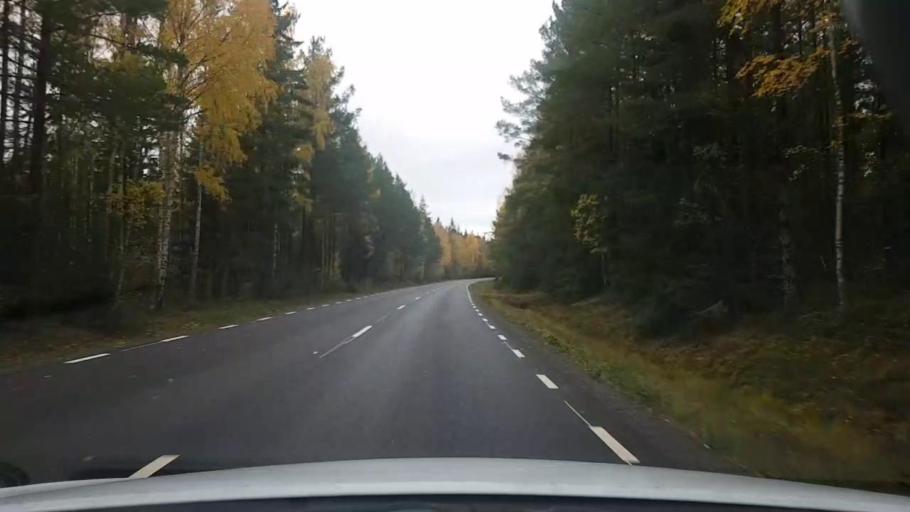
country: SE
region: OErebro
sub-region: Laxa Kommun
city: Laxa
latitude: 58.8010
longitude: 14.5424
